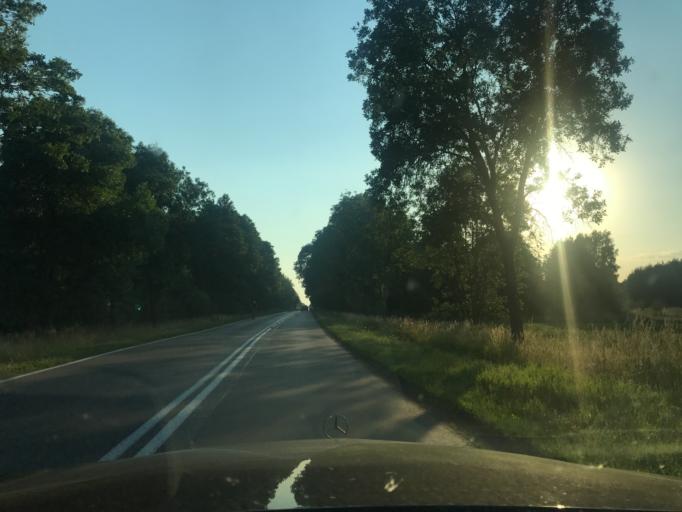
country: PL
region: Lublin Voivodeship
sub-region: Powiat parczewski
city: Debowa Kloda
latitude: 51.6452
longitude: 22.9717
